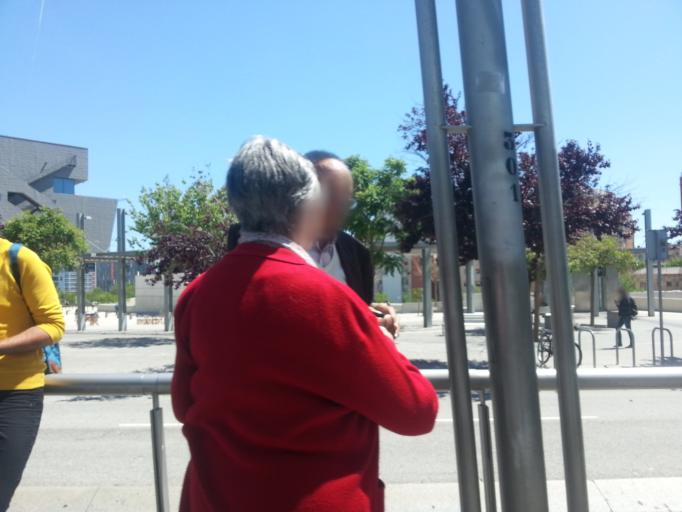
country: ES
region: Catalonia
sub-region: Provincia de Barcelona
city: Sant Marti
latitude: 41.4018
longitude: 2.1869
